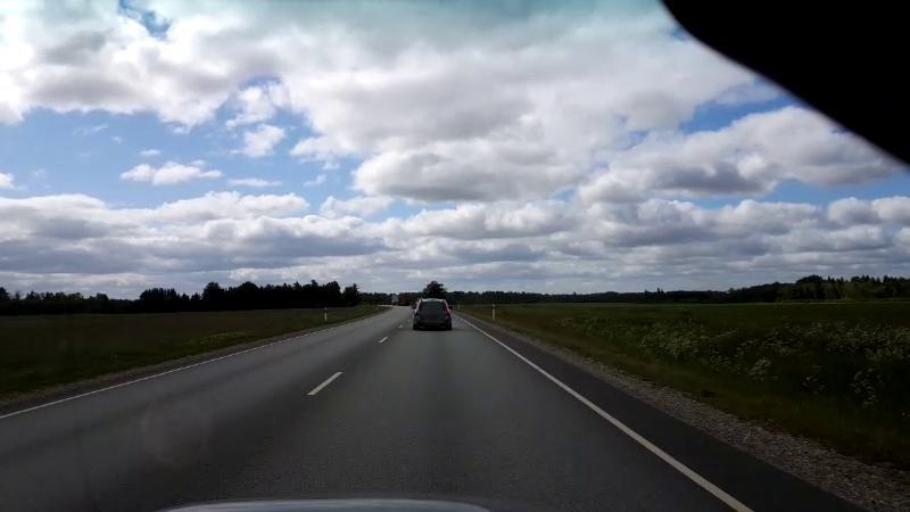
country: EE
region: Paernumaa
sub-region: Halinga vald
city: Parnu-Jaagupi
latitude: 58.5706
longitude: 24.5129
